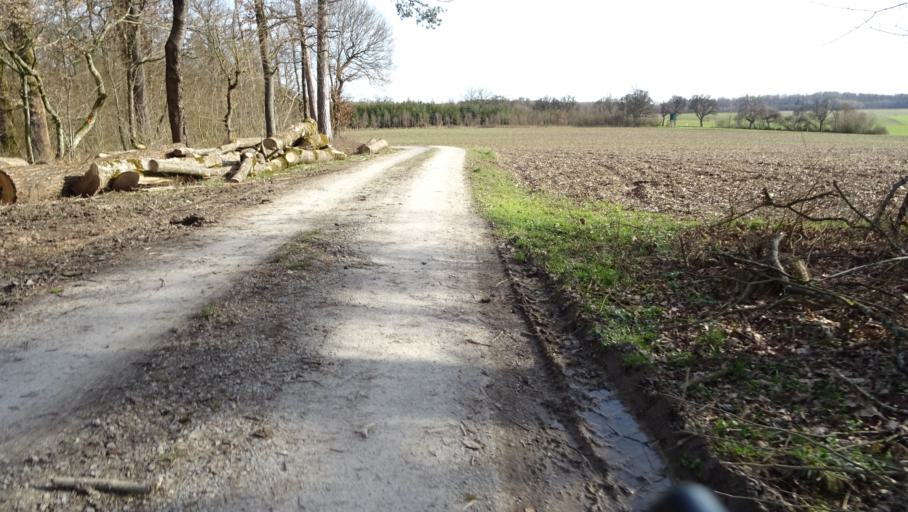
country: DE
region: Baden-Wuerttemberg
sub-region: Karlsruhe Region
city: Seckach
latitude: 49.4136
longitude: 9.3083
